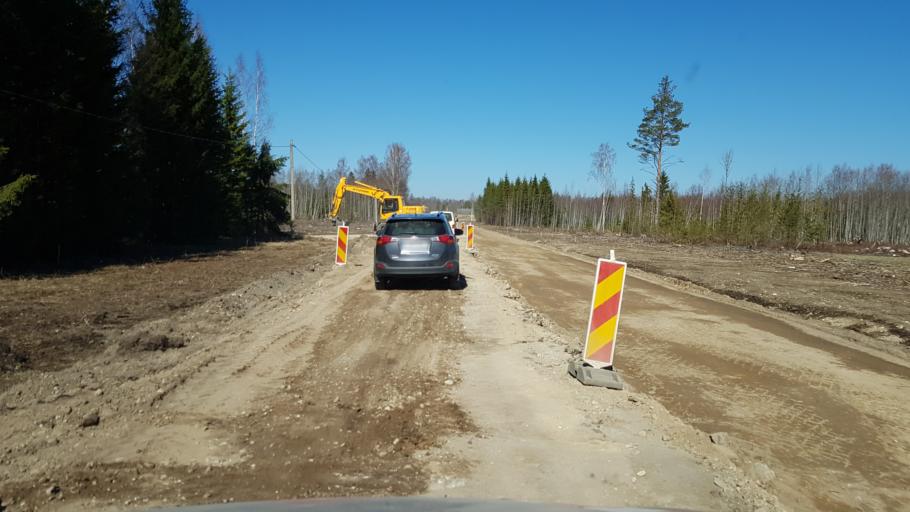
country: EE
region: Jogevamaa
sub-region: Mustvee linn
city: Mustvee
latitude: 59.0323
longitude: 26.6866
